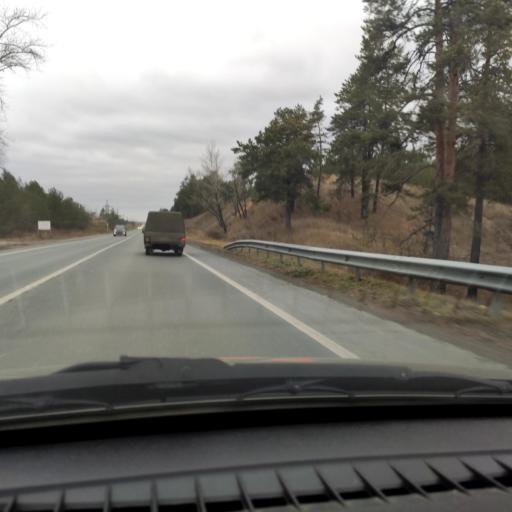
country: RU
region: Samara
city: Volzhskiy
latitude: 53.4454
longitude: 50.1006
